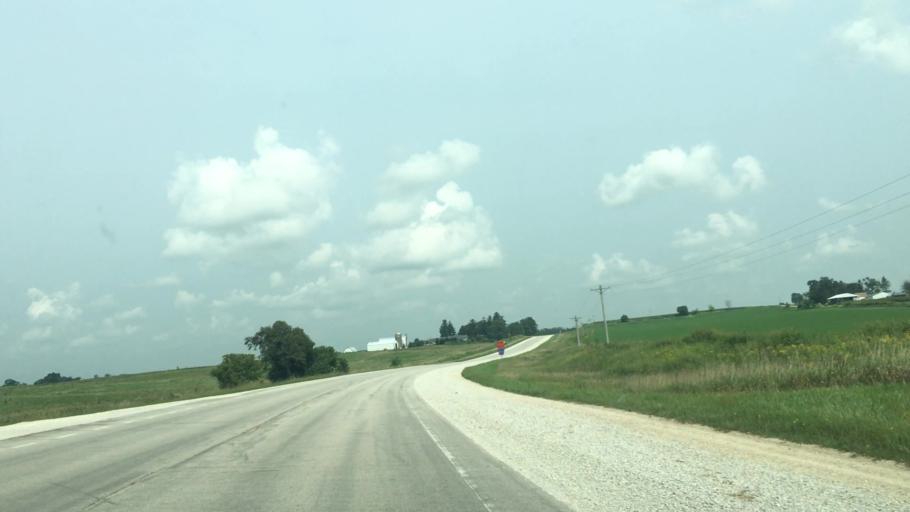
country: US
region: Iowa
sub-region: Winneshiek County
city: Decorah
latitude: 43.4142
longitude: -91.8589
